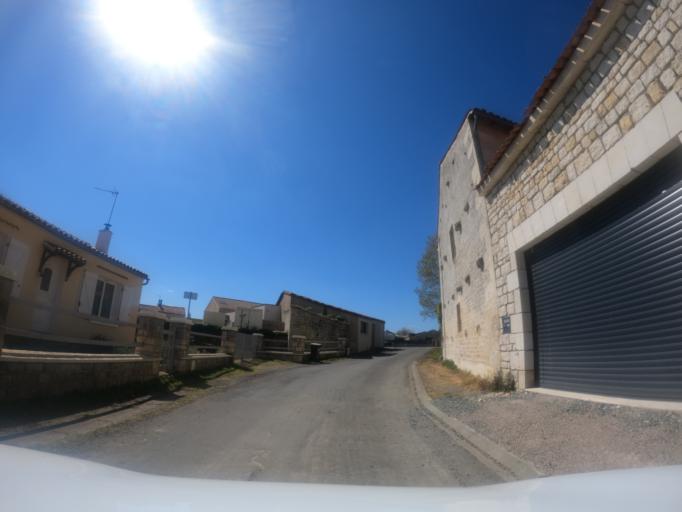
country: FR
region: Pays de la Loire
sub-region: Departement de la Vendee
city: Fontenay-le-Comte
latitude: 46.4423
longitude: -0.8669
